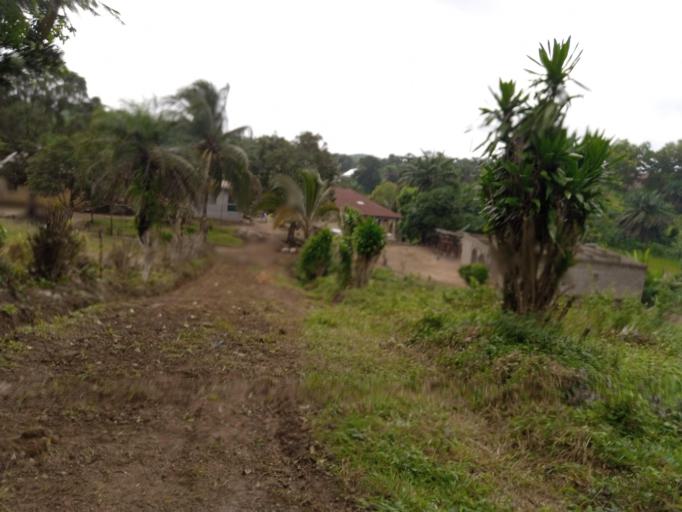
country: SL
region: Eastern Province
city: Kenema
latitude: 7.8785
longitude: -11.1740
